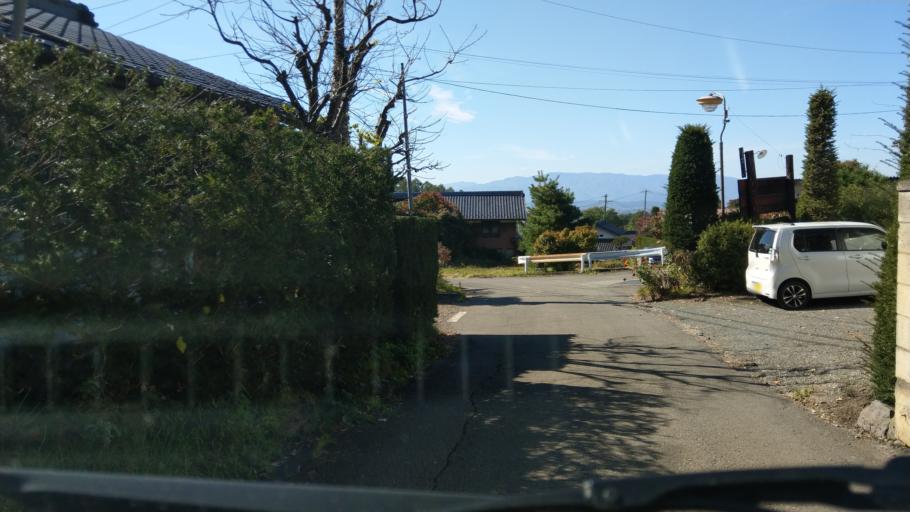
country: JP
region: Nagano
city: Komoro
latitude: 36.3653
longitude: 138.4032
